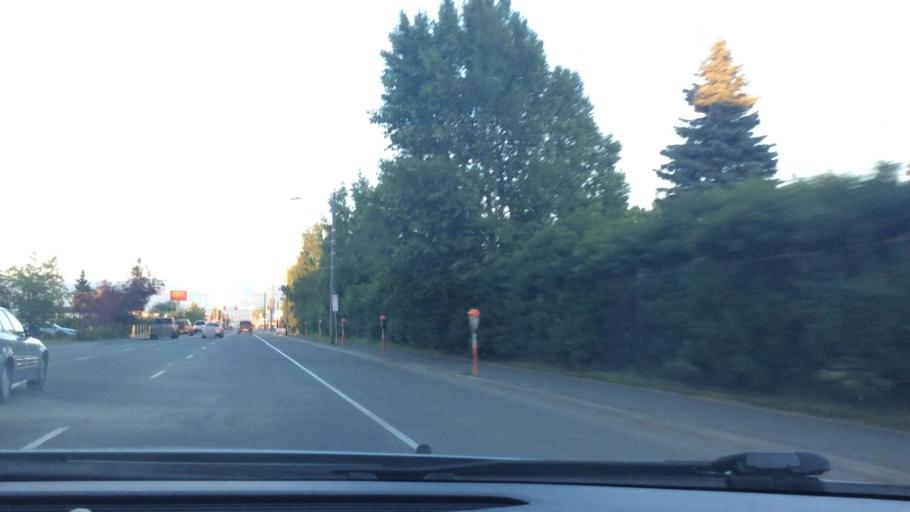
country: US
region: Alaska
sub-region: Anchorage Municipality
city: Anchorage
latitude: 61.2166
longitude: -149.8761
